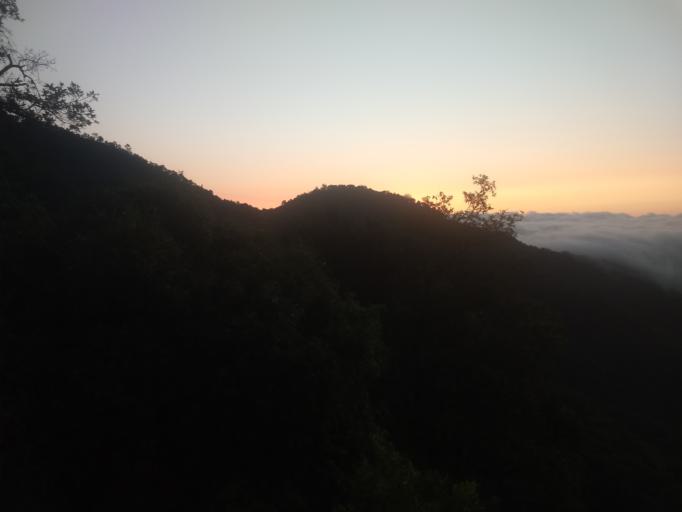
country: MX
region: Nuevo Leon
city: Santiago
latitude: 25.3533
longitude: -100.1933
